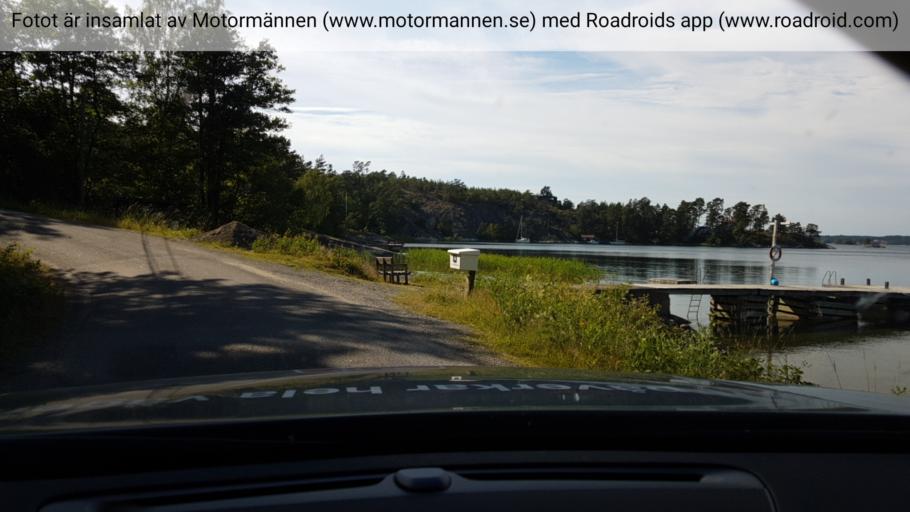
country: SE
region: Stockholm
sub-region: Haninge Kommun
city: Jordbro
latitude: 59.0173
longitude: 18.1097
